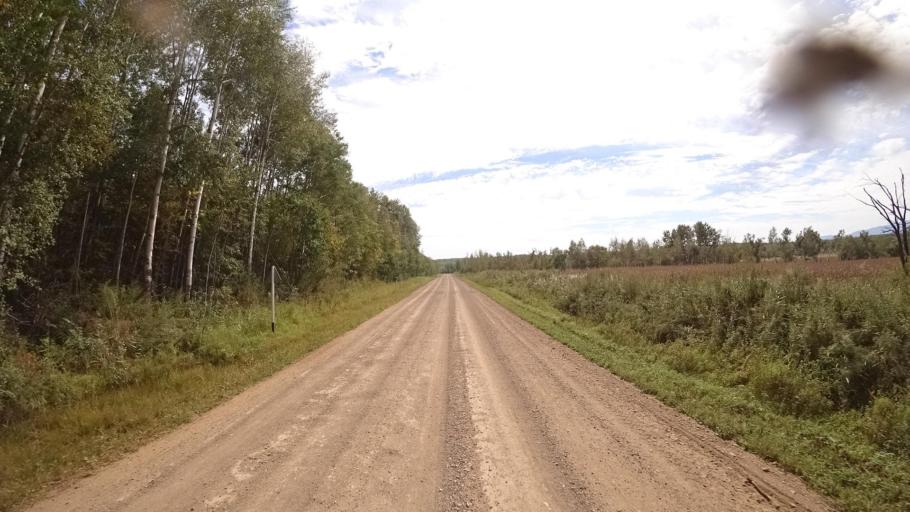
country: RU
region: Primorskiy
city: Yakovlevka
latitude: 44.5677
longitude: 133.5954
